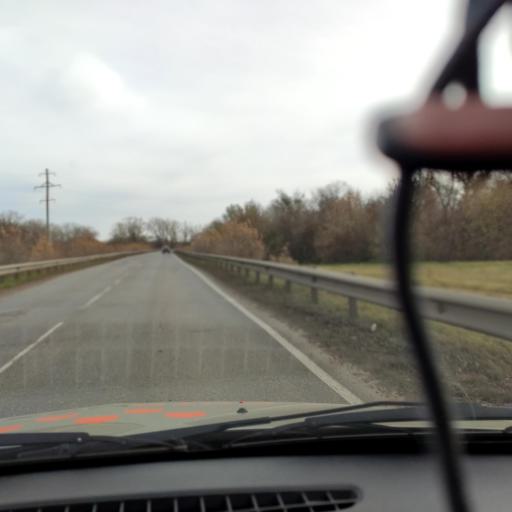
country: RU
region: Bashkortostan
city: Ufa
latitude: 54.5702
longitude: 55.9691
